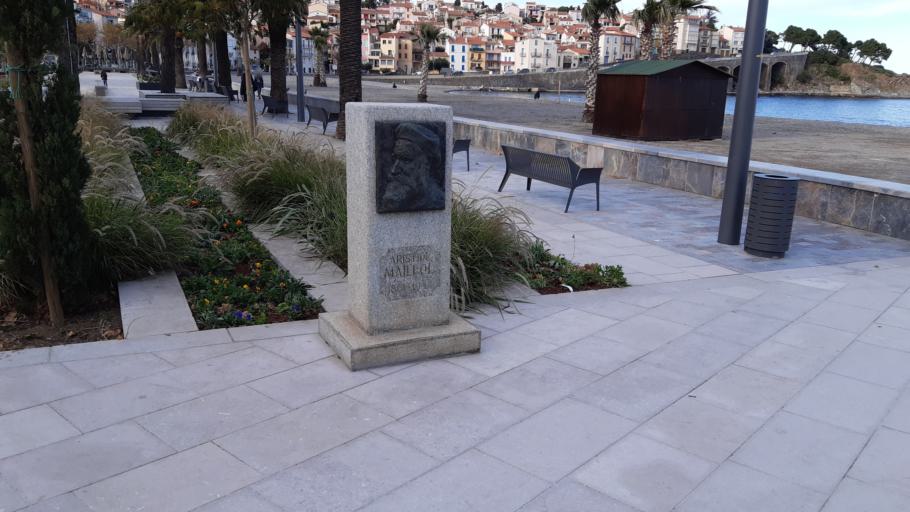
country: FR
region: Languedoc-Roussillon
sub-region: Departement des Pyrenees-Orientales
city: Banyuls de la Marenda
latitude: 42.4812
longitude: 3.1300
